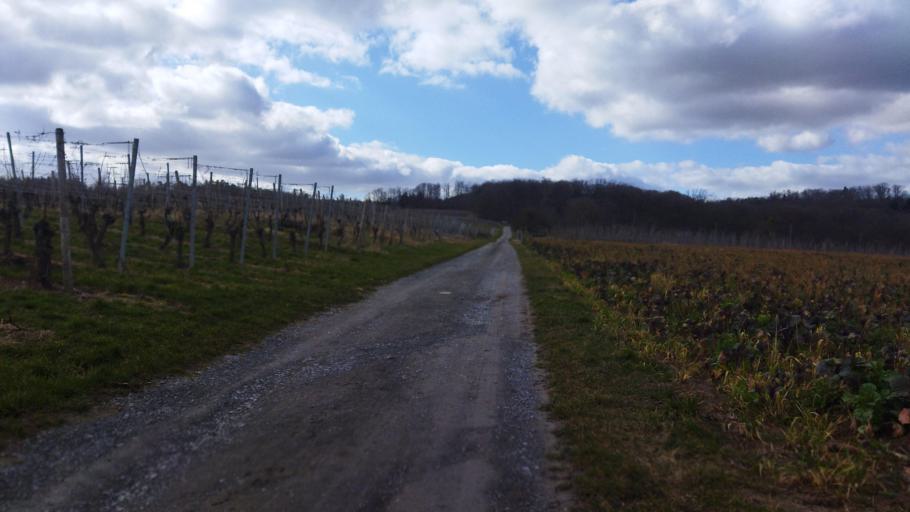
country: DE
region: Baden-Wuerttemberg
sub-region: Regierungsbezirk Stuttgart
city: Erligheim
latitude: 49.0139
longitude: 9.0822
